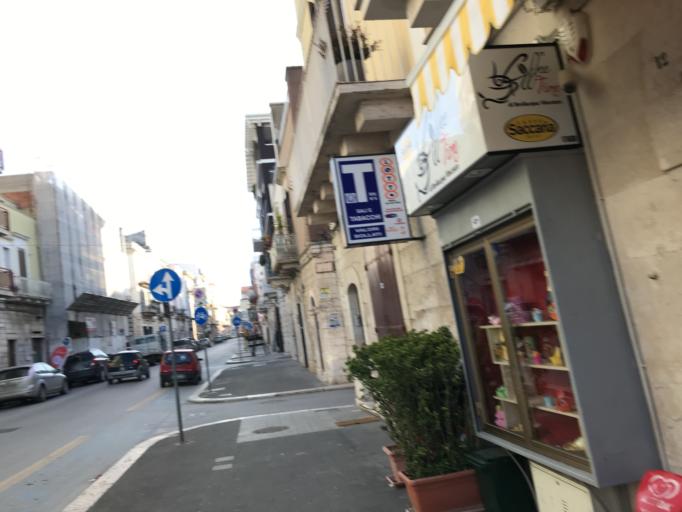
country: IT
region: Apulia
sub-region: Provincia di Bari
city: Corato
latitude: 41.1508
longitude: 16.4121
